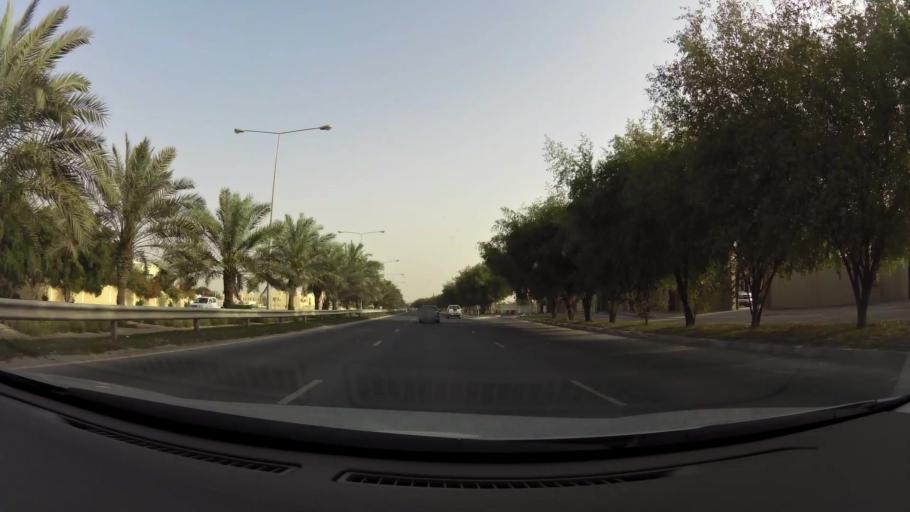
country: QA
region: Baladiyat ar Rayyan
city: Ar Rayyan
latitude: 25.2515
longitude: 51.4585
